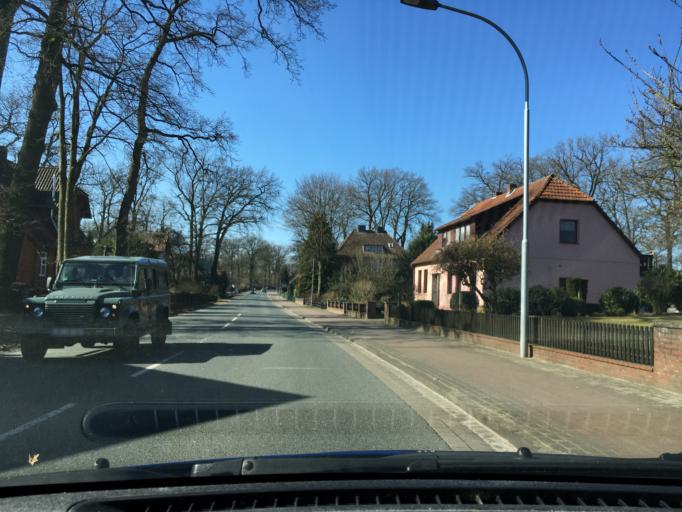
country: DE
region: Lower Saxony
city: Neuenkirchen
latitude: 53.0670
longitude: 9.6672
